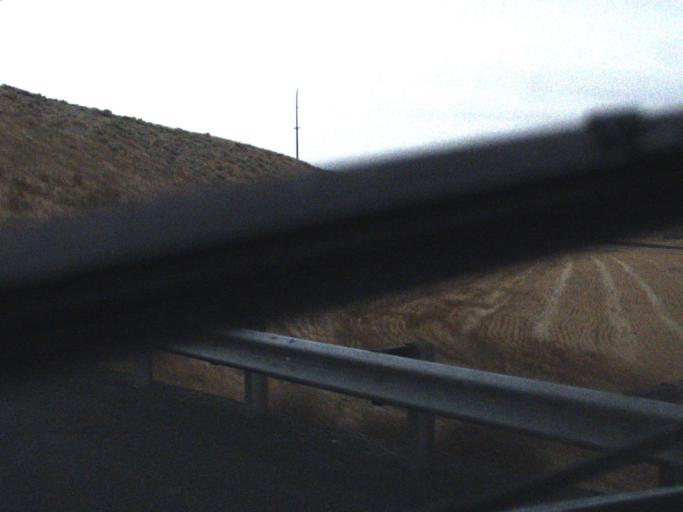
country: US
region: Washington
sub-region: Adams County
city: Ritzville
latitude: 46.7827
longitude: -118.3827
